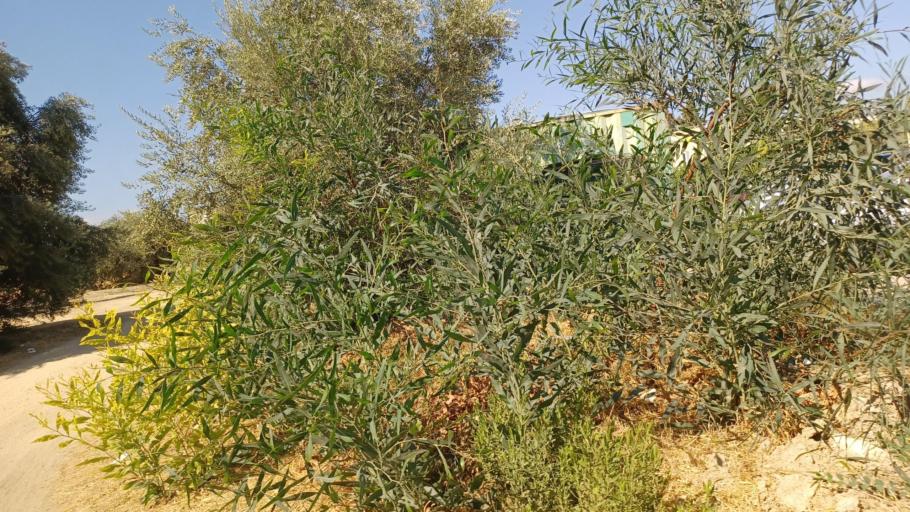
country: CY
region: Pafos
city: Polis
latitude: 35.0357
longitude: 32.4310
